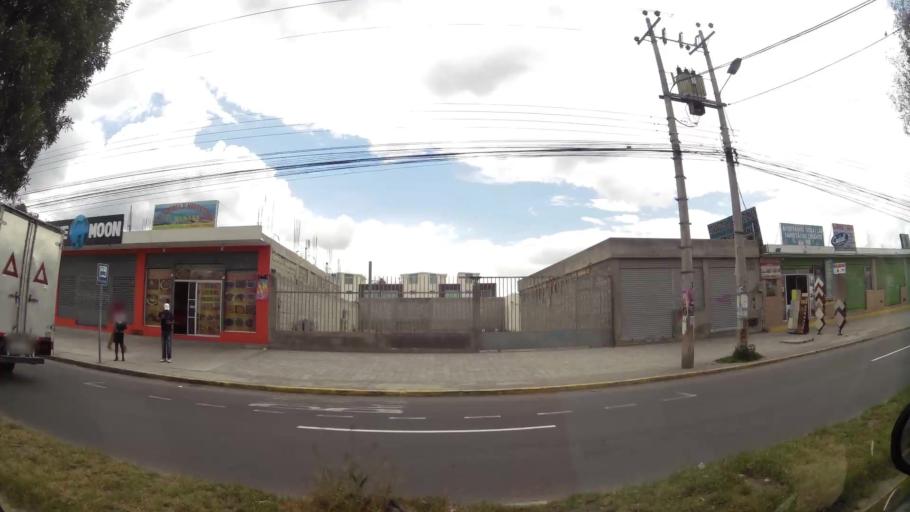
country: EC
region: Pichincha
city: Quito
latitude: -0.0852
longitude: -78.4208
